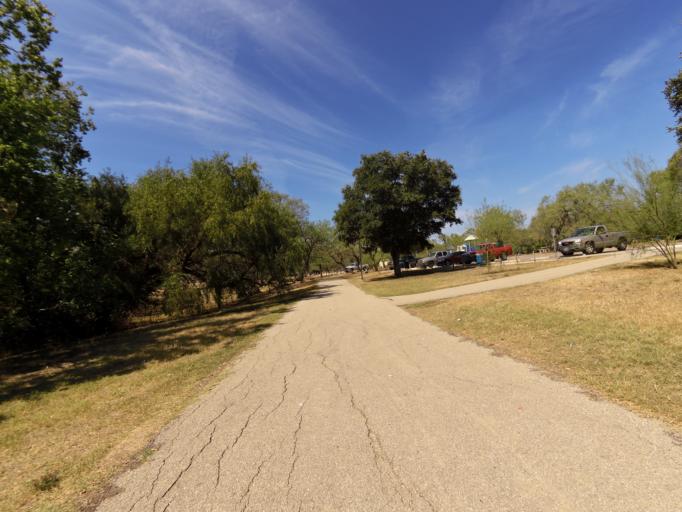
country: US
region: Texas
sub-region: Bexar County
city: San Antonio
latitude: 29.3858
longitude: -98.4284
